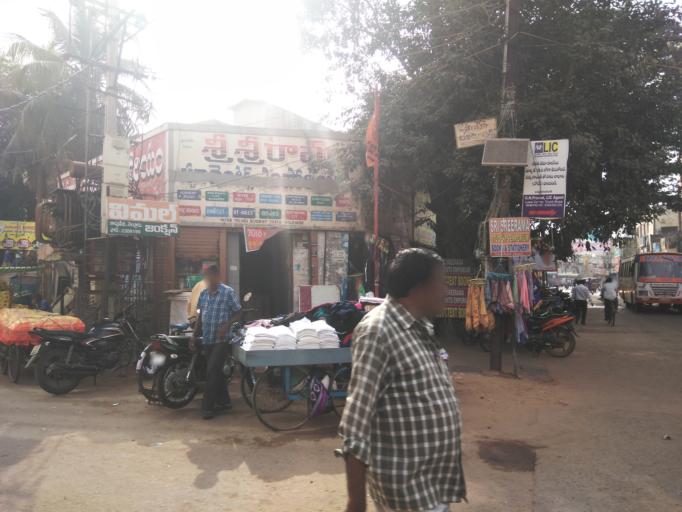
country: IN
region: Andhra Pradesh
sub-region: Nellore
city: Nellore
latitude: 14.4534
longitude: 79.9839
